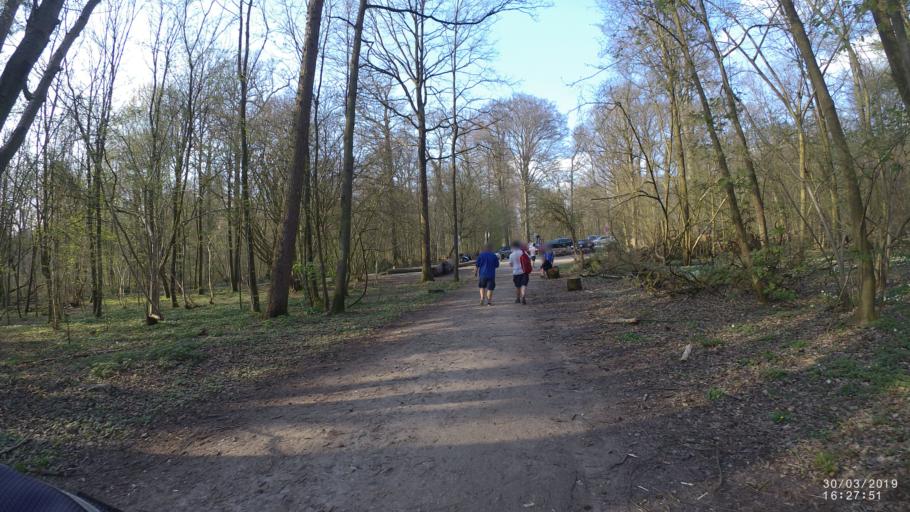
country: BE
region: Flanders
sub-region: Provincie Vlaams-Brabant
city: Kraainem
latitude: 50.8147
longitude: 4.4494
